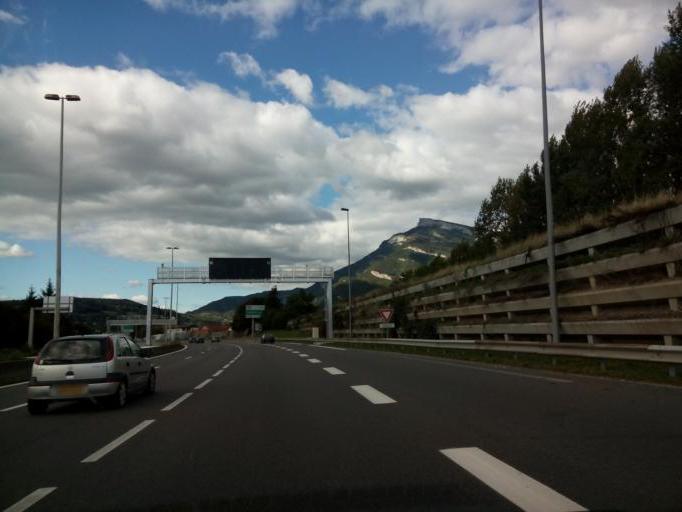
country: FR
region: Rhone-Alpes
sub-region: Departement de la Savoie
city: Chambery
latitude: 45.5616
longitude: 5.9488
